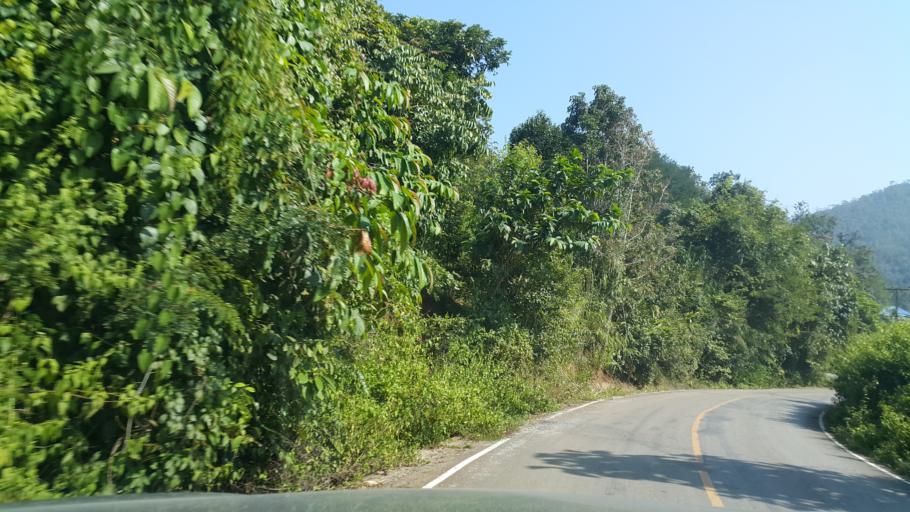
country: TH
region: Chiang Mai
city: Samoeng
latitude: 18.8802
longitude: 98.6090
